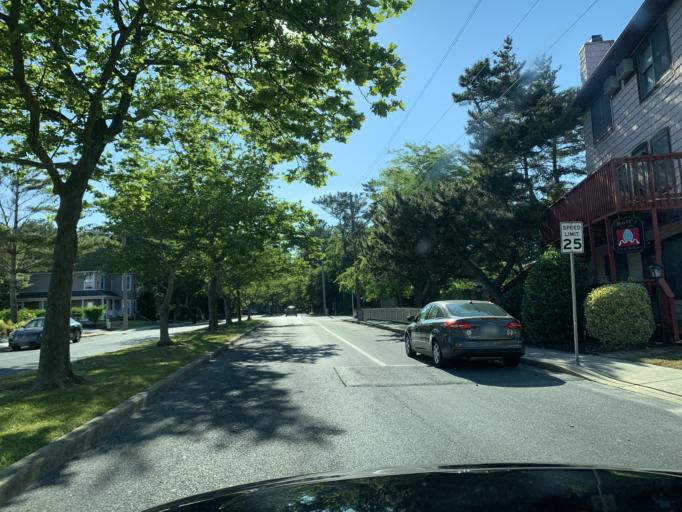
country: US
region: Delaware
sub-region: Sussex County
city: Bethany Beach
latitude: 38.4476
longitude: -75.0556
